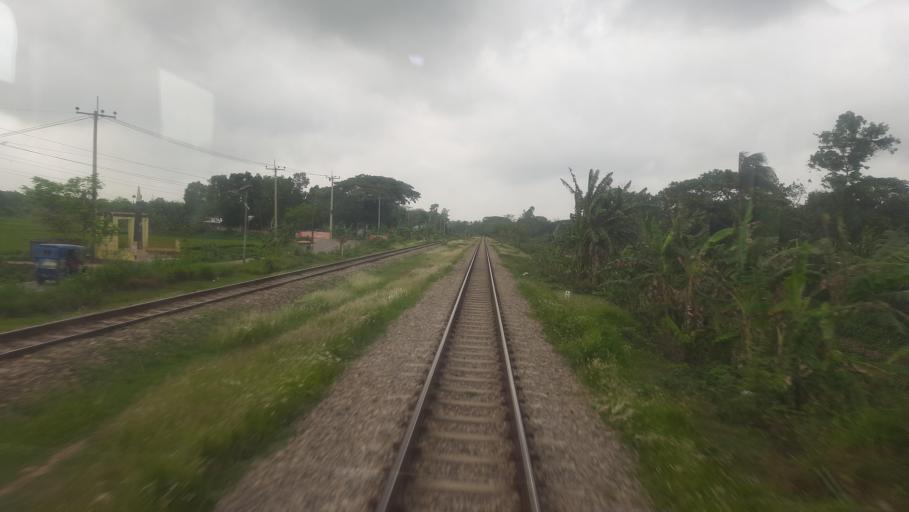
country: BD
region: Dhaka
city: Narsingdi
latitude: 23.9640
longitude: 90.8142
